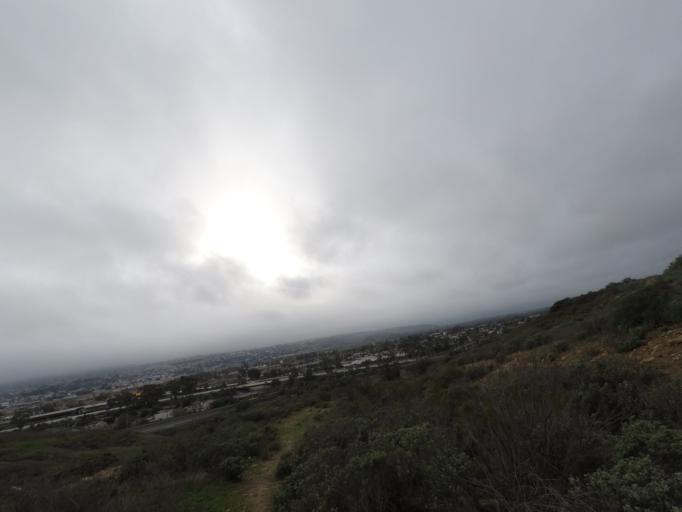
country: MX
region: Baja California
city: Tijuana
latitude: 32.5547
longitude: -117.0367
